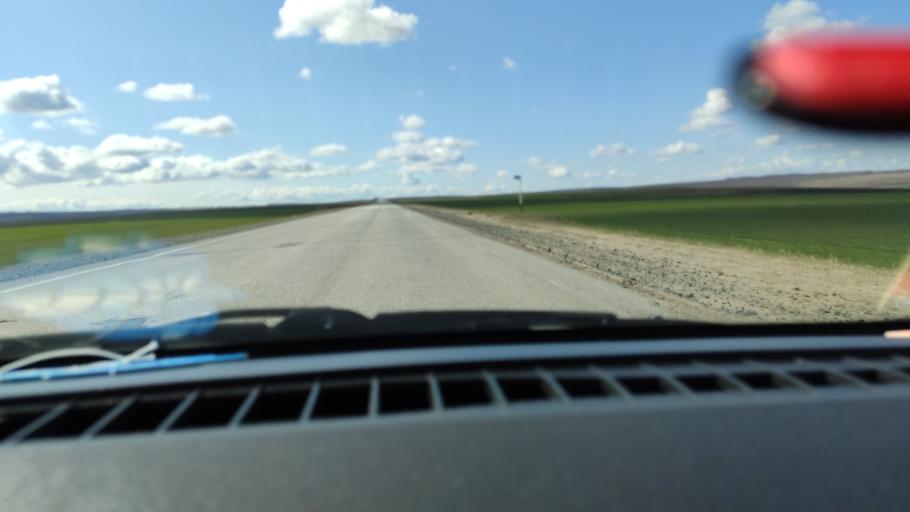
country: RU
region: Samara
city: Varlamovo
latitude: 53.0418
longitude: 48.3396
